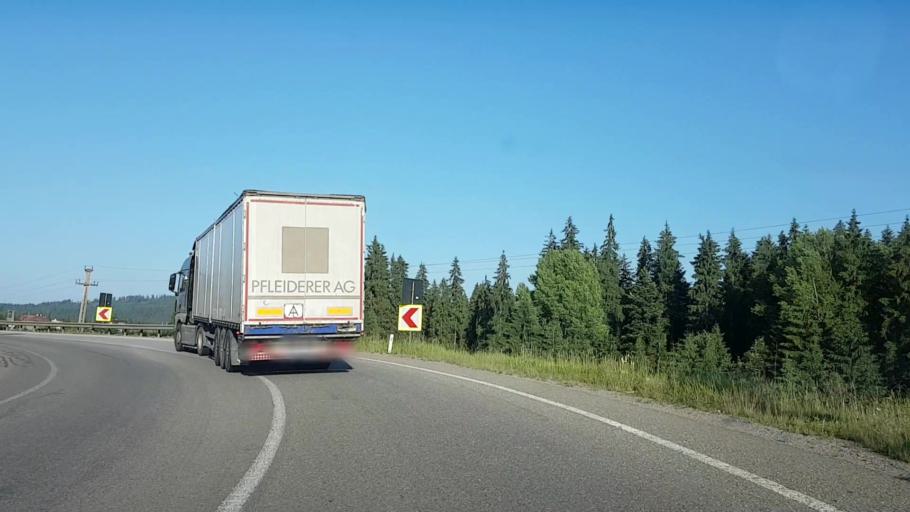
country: RO
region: Suceava
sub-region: Comuna Poiana Stampei
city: Poiana Stampei
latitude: 47.2998
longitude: 25.0976
